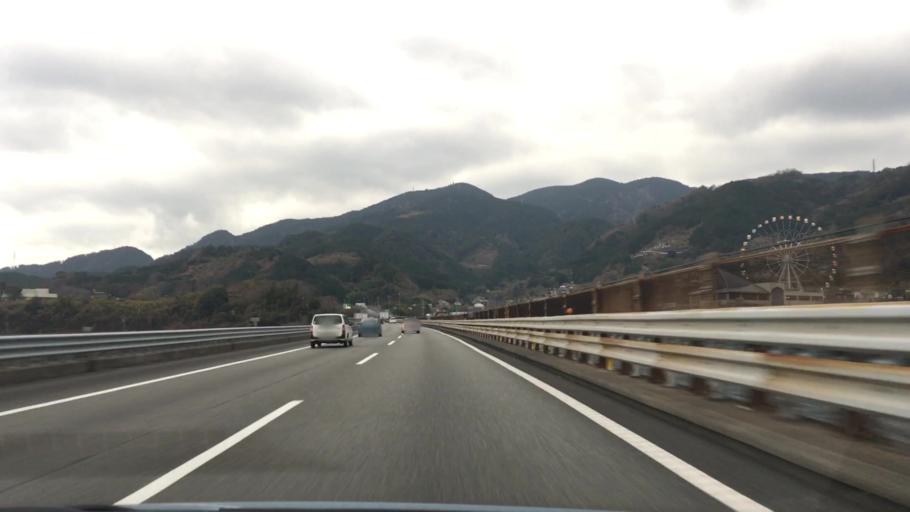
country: JP
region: Shizuoka
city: Fujinomiya
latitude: 35.1629
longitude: 138.6235
